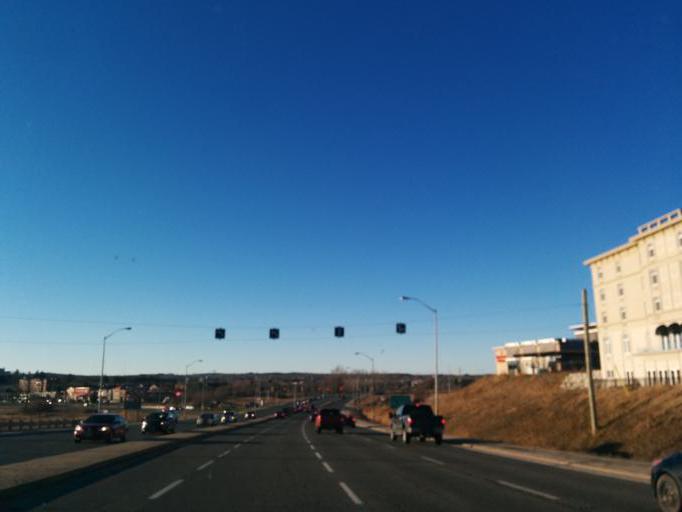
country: CA
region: Ontario
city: Orangeville
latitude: 43.9208
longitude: -80.0806
